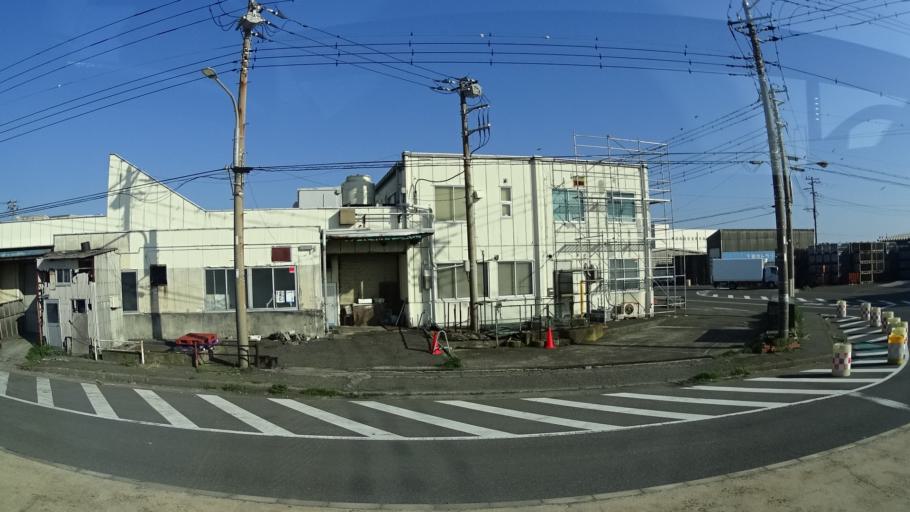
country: JP
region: Kanagawa
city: Miura
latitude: 35.1432
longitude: 139.6117
